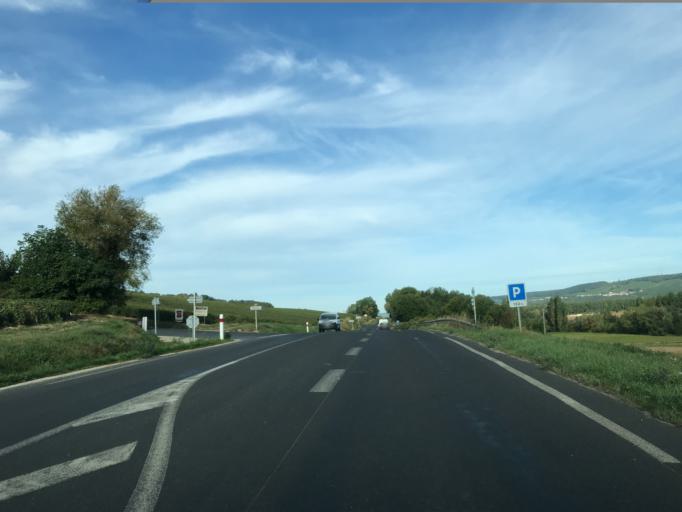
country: FR
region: Champagne-Ardenne
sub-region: Departement de la Marne
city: Damery
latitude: 49.0567
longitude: 3.8924
